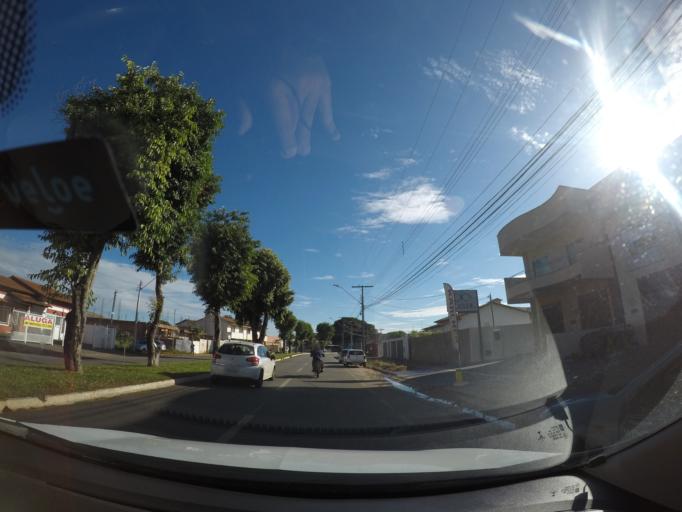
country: BR
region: Goias
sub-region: Goiania
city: Goiania
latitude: -16.7299
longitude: -49.3050
